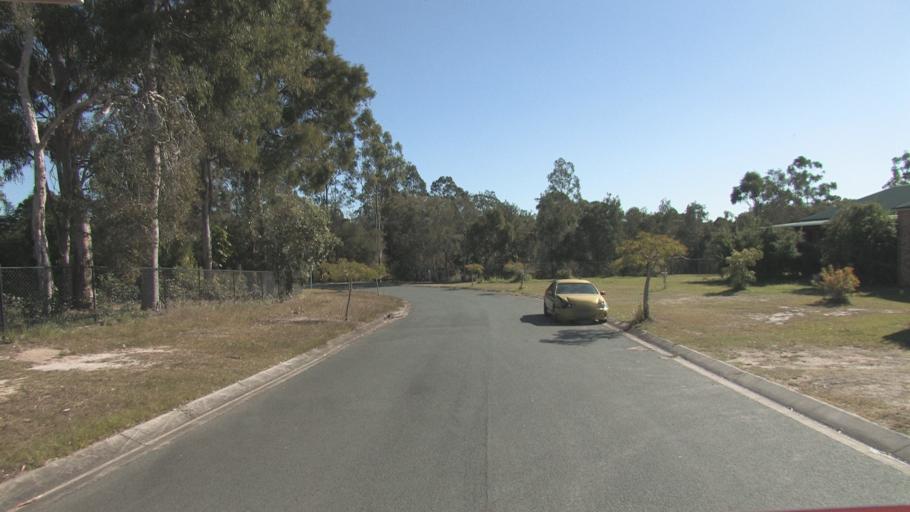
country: AU
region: Queensland
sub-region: Brisbane
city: Forest Lake
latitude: -27.6646
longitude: 153.0173
